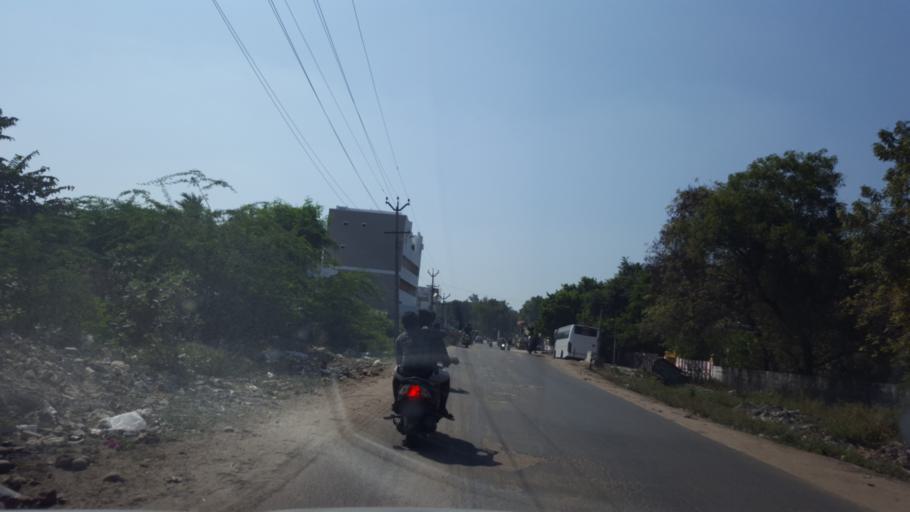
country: IN
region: Tamil Nadu
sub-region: Kancheepuram
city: Kanchipuram
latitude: 12.8392
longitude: 79.7155
